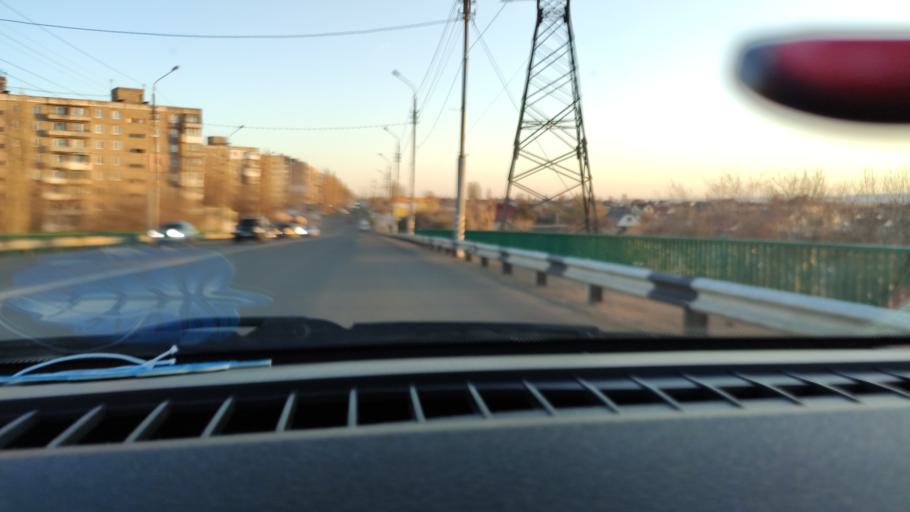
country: RU
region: Saratov
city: Privolzhskiy
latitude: 51.4120
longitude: 46.0424
